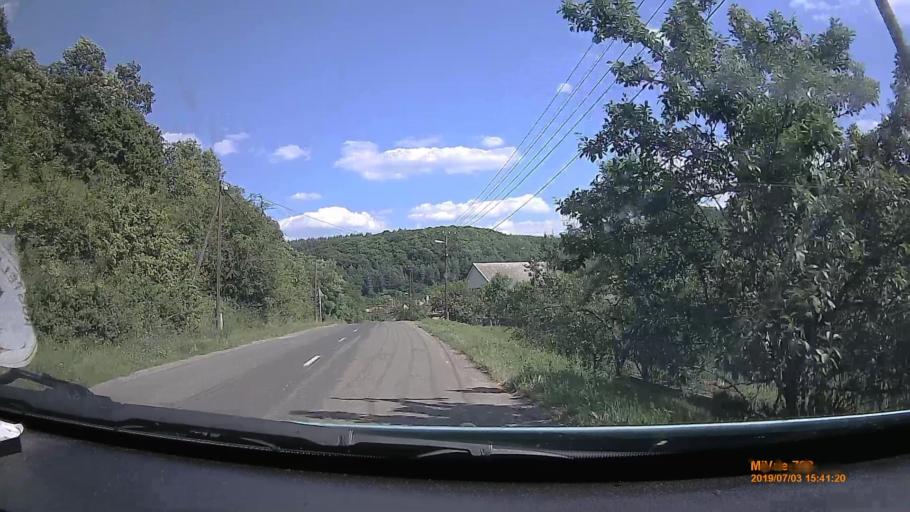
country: HU
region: Heves
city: Szilvasvarad
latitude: 48.1677
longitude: 20.4214
